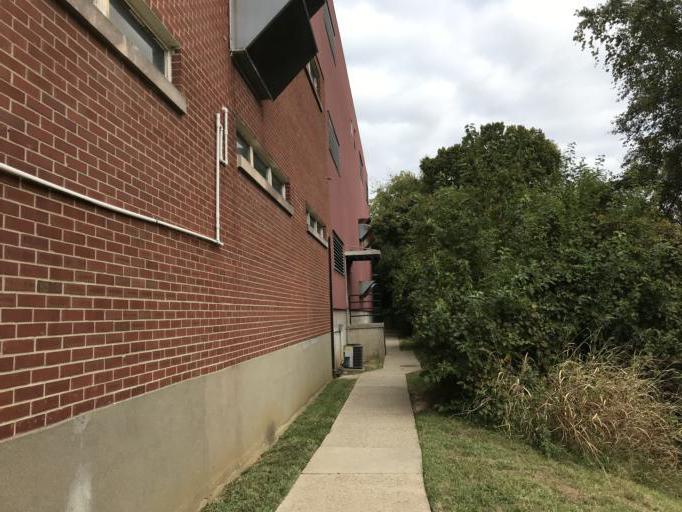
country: US
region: Indiana
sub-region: Clark County
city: Jeffersonville
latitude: 38.2580
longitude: -85.7136
